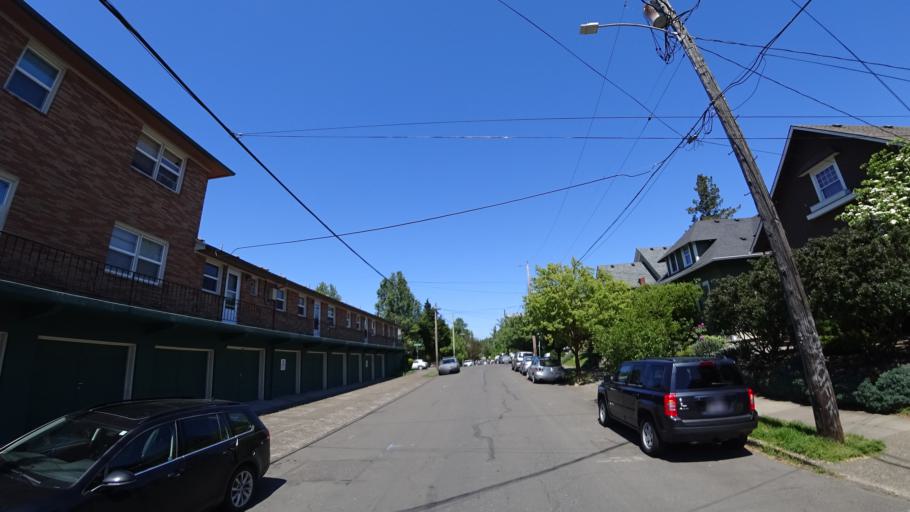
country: US
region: Oregon
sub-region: Multnomah County
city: Portland
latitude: 45.5124
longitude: -122.6283
